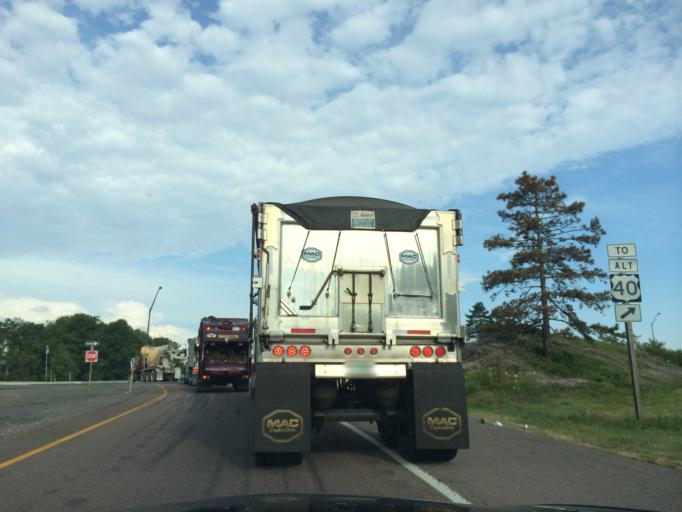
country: US
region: Maryland
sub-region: Allegany County
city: Frostburg
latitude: 39.6336
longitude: -78.9173
